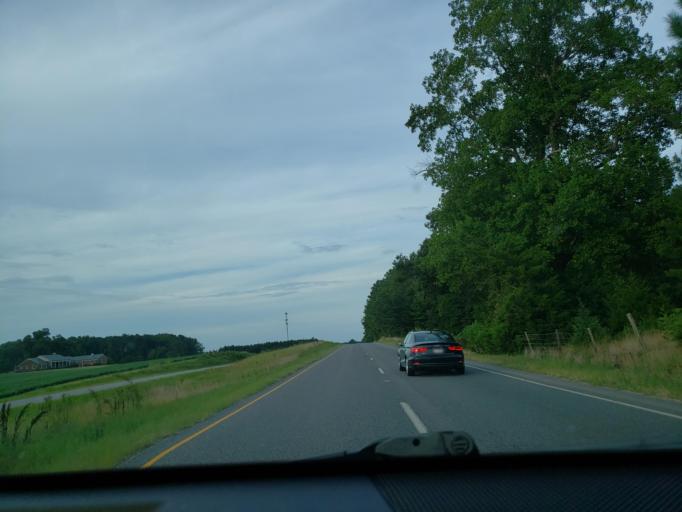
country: US
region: Virginia
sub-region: Brunswick County
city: Lawrenceville
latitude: 36.7336
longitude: -77.9057
